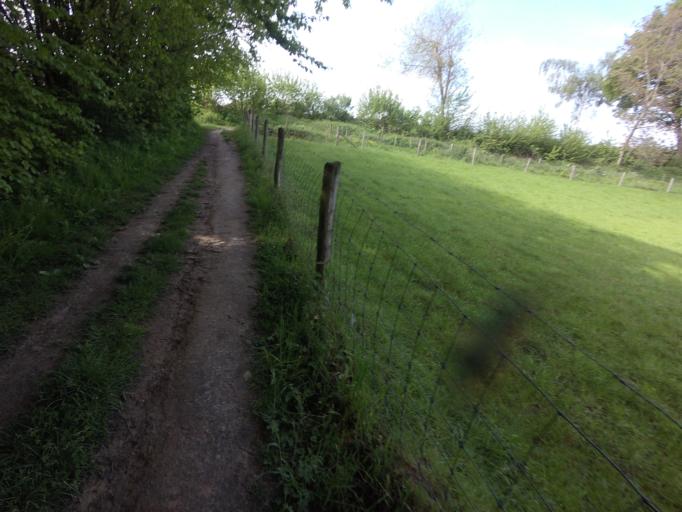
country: NL
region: Limburg
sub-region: Valkenburg aan de Geul
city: Berg
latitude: 50.8476
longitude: 5.7762
